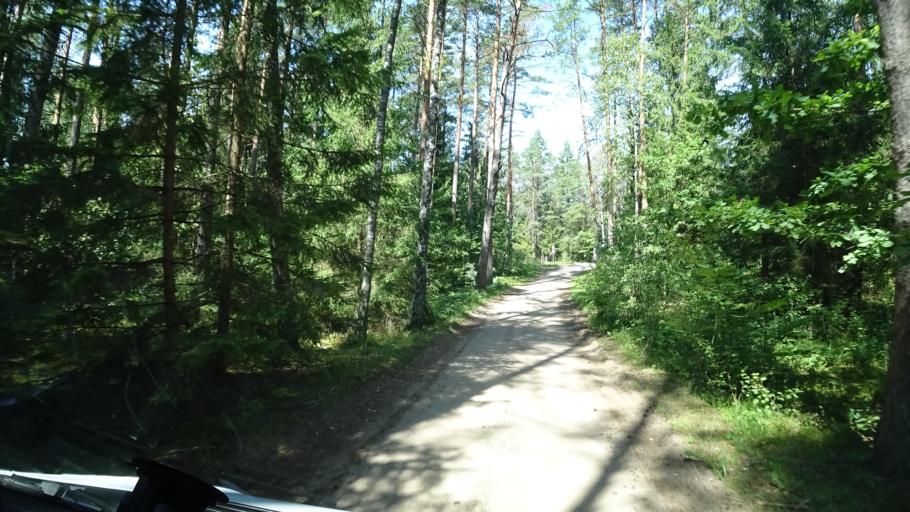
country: LT
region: Vilnius County
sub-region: Trakai
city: Rudiskes
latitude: 54.5089
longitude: 24.8895
